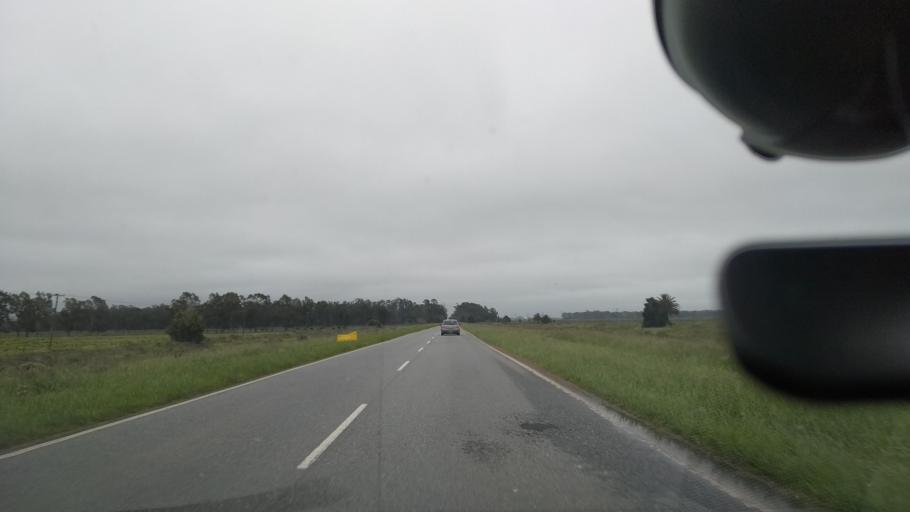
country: AR
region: Buenos Aires
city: Veronica
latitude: -35.3239
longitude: -57.4728
